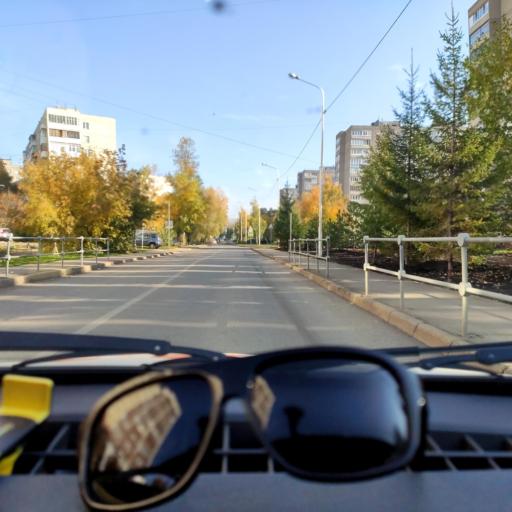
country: RU
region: Bashkortostan
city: Ufa
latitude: 54.6986
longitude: 55.9978
